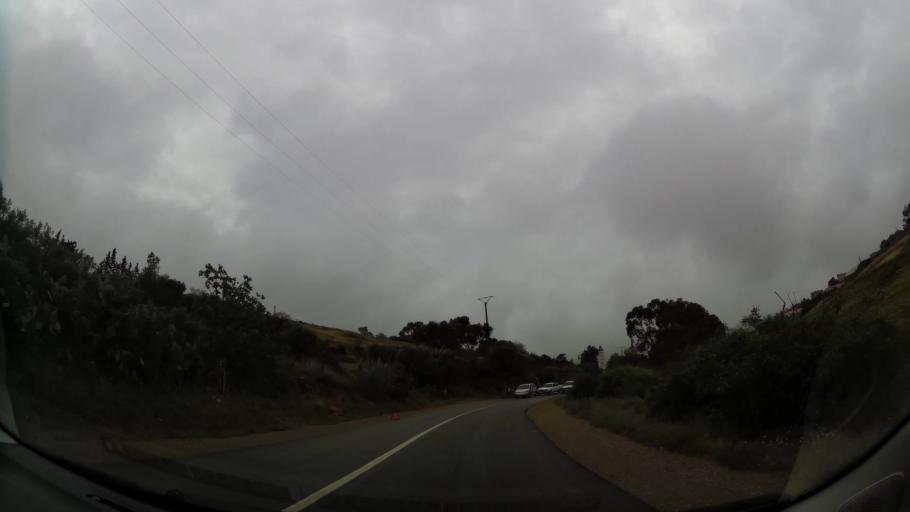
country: MA
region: Oriental
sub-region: Nador
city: Nador
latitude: 35.1316
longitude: -3.0556
